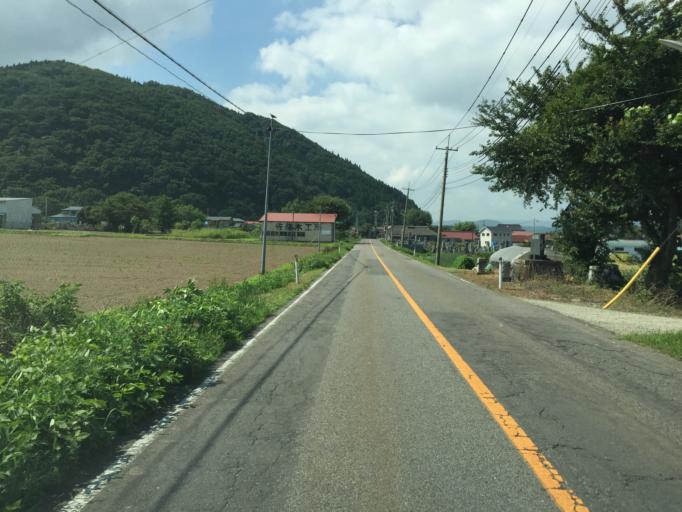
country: JP
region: Fukushima
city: Inawashiro
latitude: 37.4415
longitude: 140.1514
